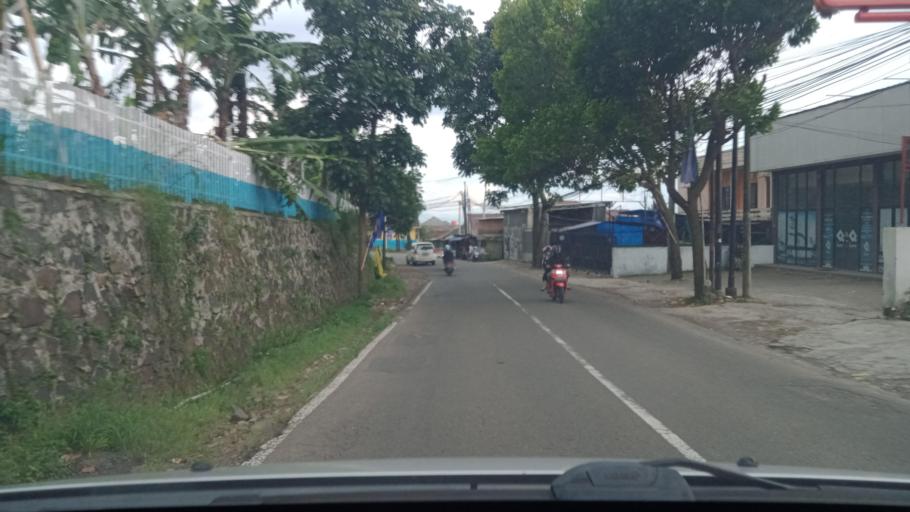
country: ID
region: West Java
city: Lembang
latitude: -6.8030
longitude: 107.5806
